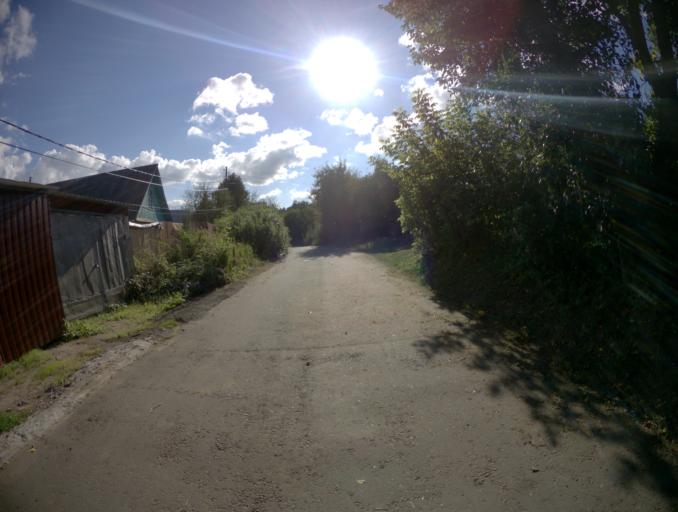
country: RU
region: Vladimir
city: Vladimir
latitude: 56.1178
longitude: 40.3813
